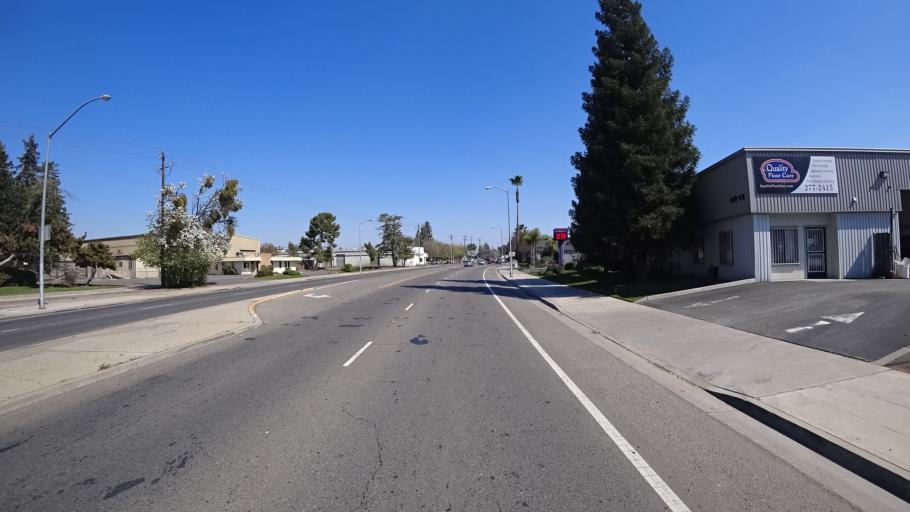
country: US
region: California
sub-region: Fresno County
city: West Park
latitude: 36.7935
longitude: -119.8558
